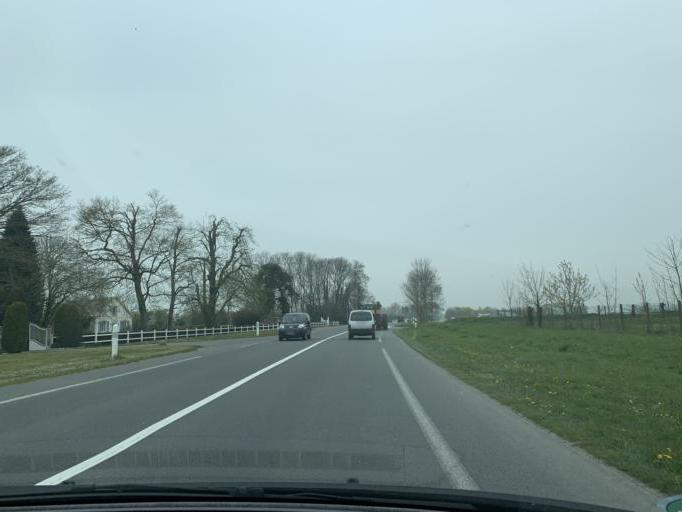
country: FR
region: Picardie
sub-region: Departement de la Somme
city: Abbeville
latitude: 50.1360
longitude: 1.8260
